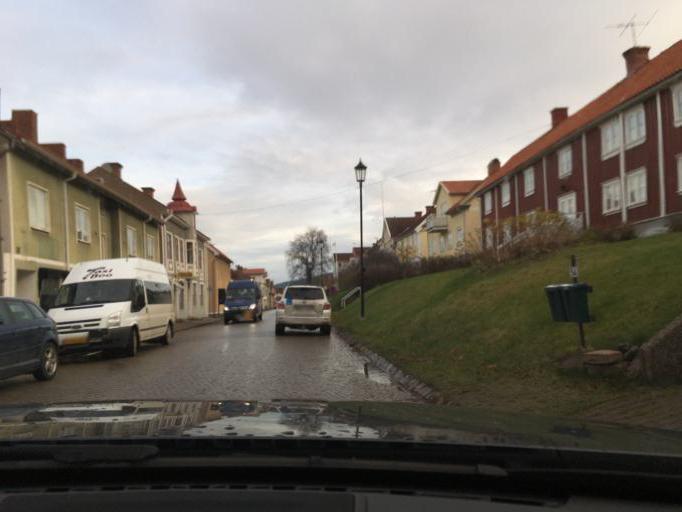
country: SE
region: Joenkoeping
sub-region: Jonkopings Kommun
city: Graenna
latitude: 58.0240
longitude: 14.4689
